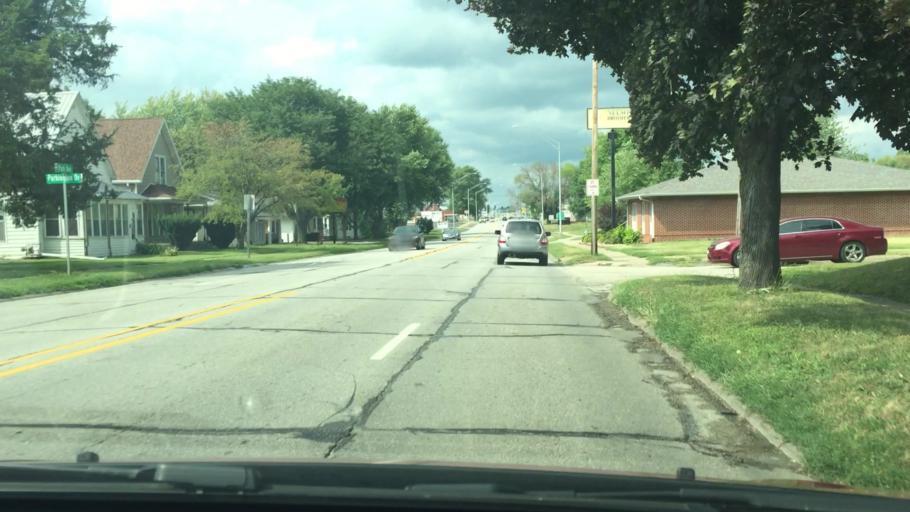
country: US
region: Iowa
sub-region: Muscatine County
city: Muscatine
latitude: 41.4384
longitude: -91.0307
